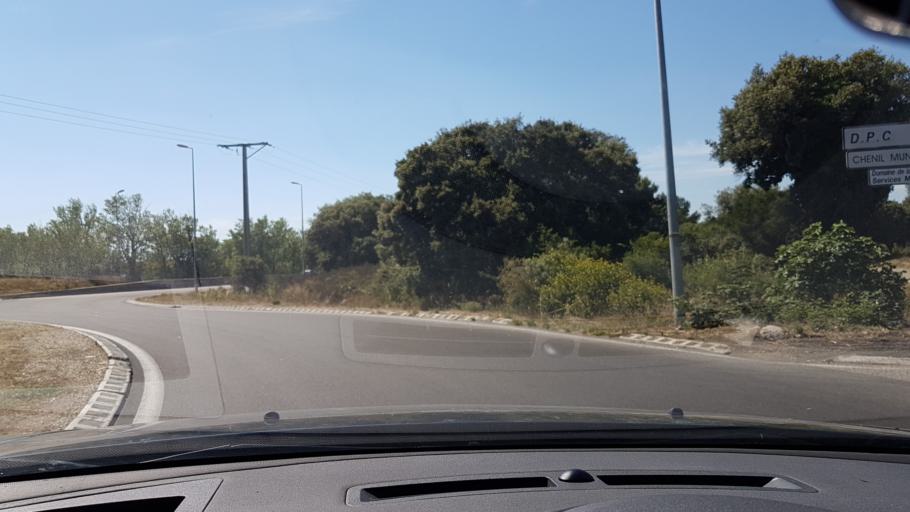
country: FR
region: Provence-Alpes-Cote d'Azur
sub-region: Departement des Bouches-du-Rhone
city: Fos-sur-Mer
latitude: 43.4620
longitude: 4.9200
